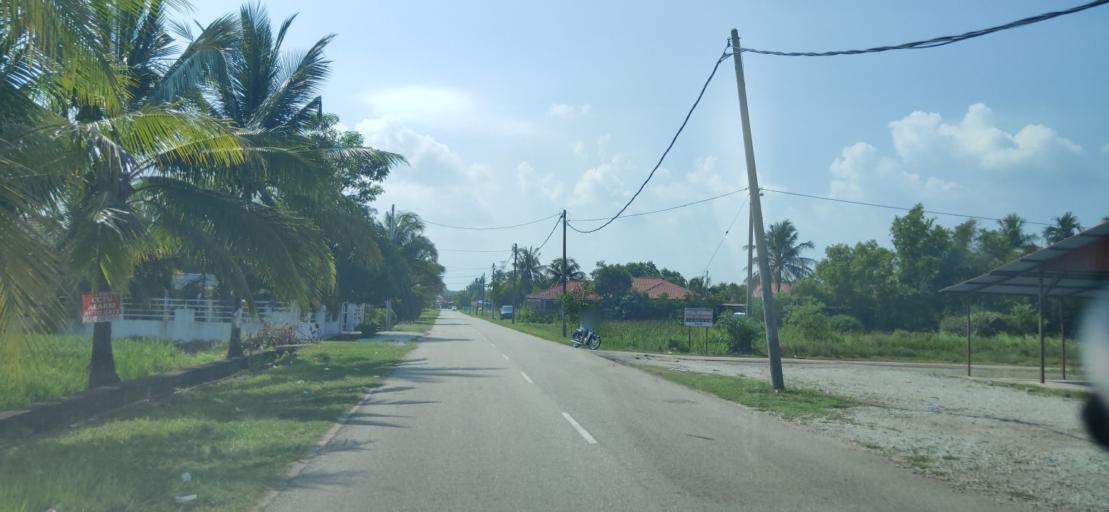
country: MY
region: Kedah
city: Sungai Petani
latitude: 5.6604
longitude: 100.4662
